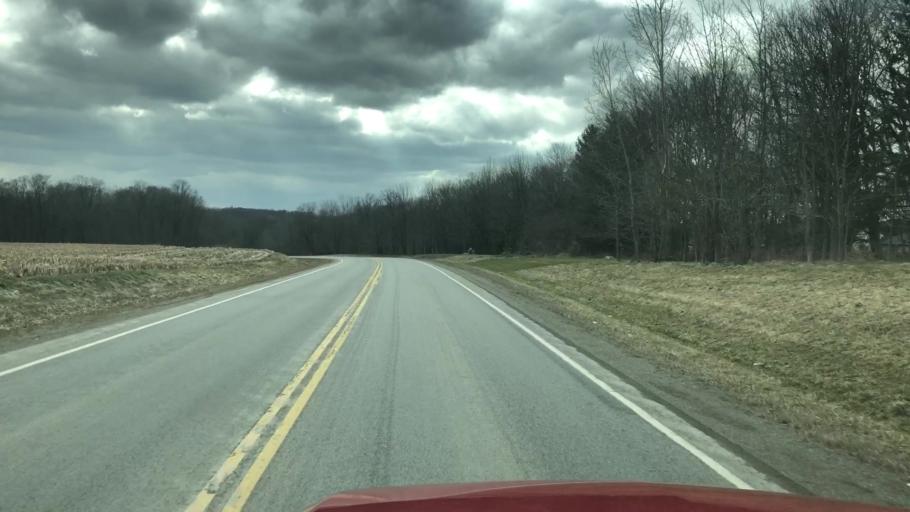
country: US
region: New York
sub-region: Monroe County
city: Fairport
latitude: 43.1308
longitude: -77.3630
